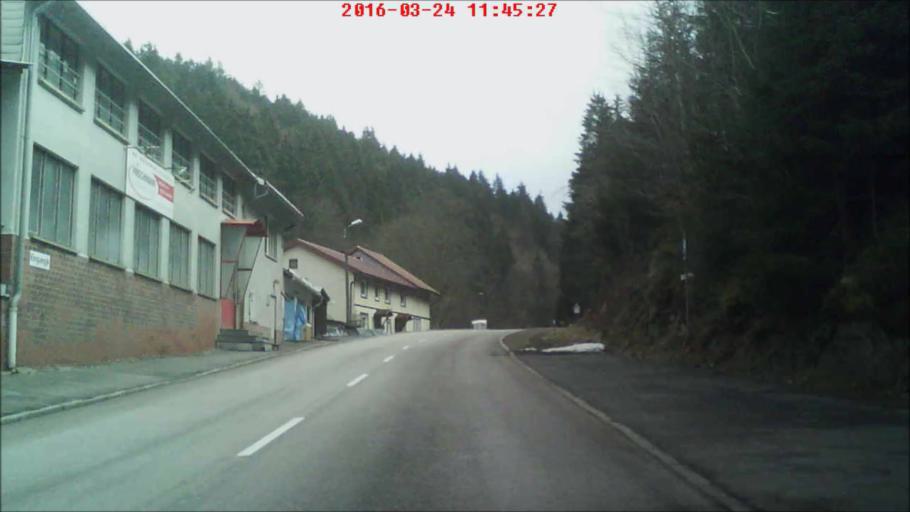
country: DE
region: Thuringia
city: Bachfeld
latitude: 50.4584
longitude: 10.9906
